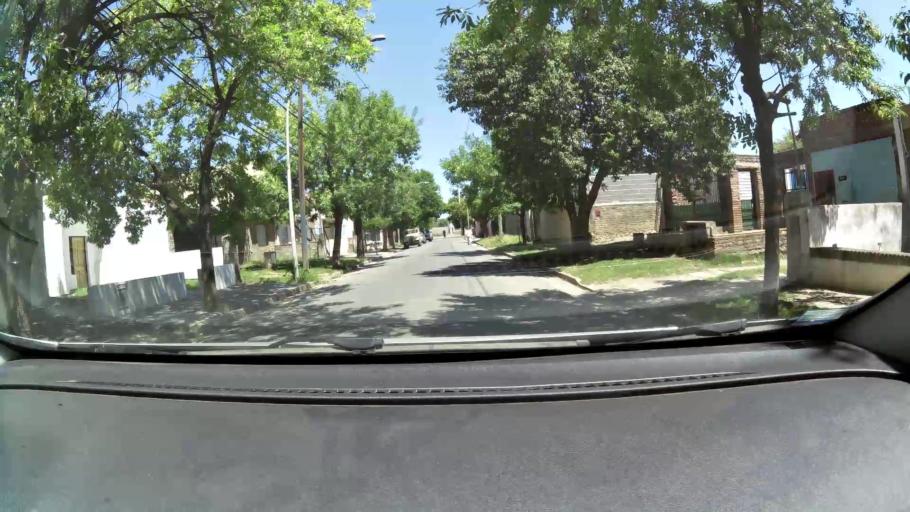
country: AR
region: Cordoba
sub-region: Departamento de Capital
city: Cordoba
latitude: -31.4364
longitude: -64.1224
